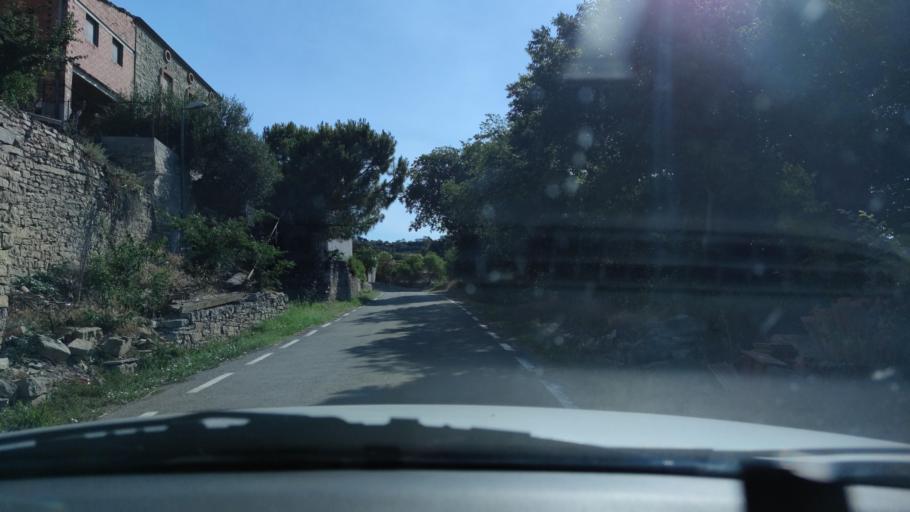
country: ES
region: Catalonia
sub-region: Provincia de Lleida
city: Ivorra
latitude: 41.7375
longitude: 1.3503
